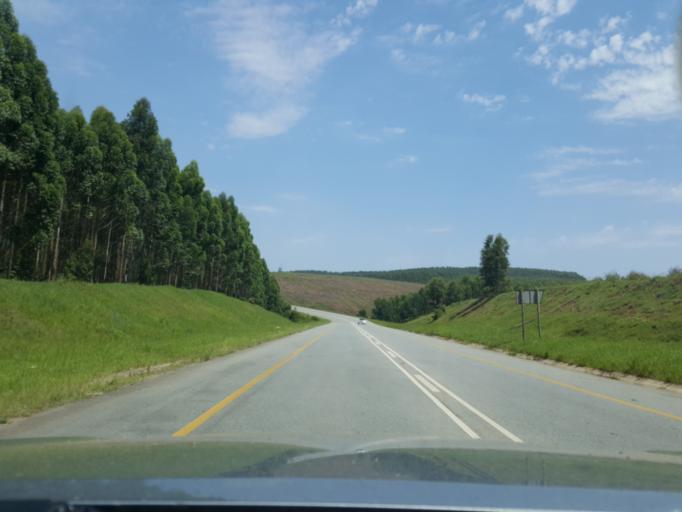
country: ZA
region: Mpumalanga
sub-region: Ehlanzeni District
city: White River
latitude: -25.1985
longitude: 31.0359
